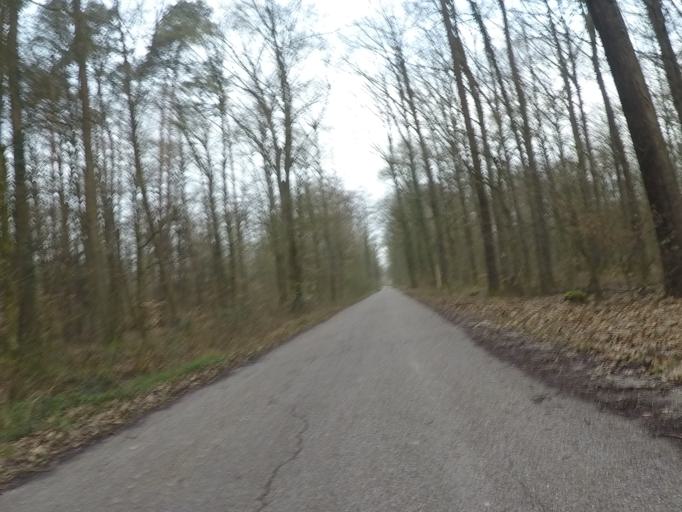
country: DE
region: Rheinland-Pfalz
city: Kandel
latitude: 49.0728
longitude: 8.2140
